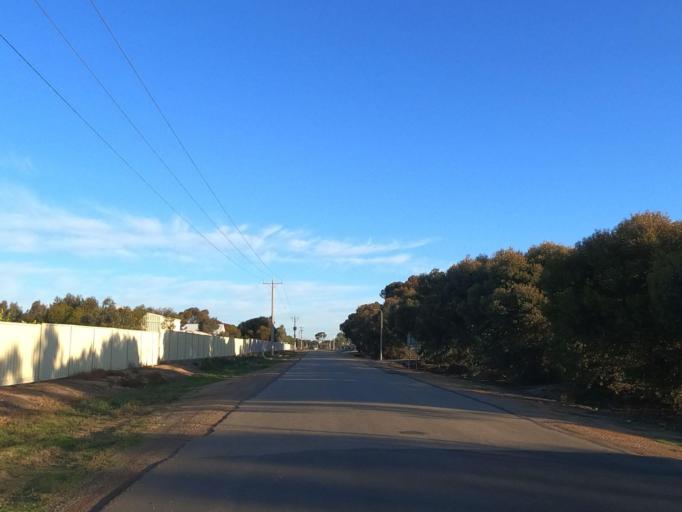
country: AU
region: Victoria
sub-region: Swan Hill
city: Swan Hill
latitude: -35.3301
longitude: 143.5346
